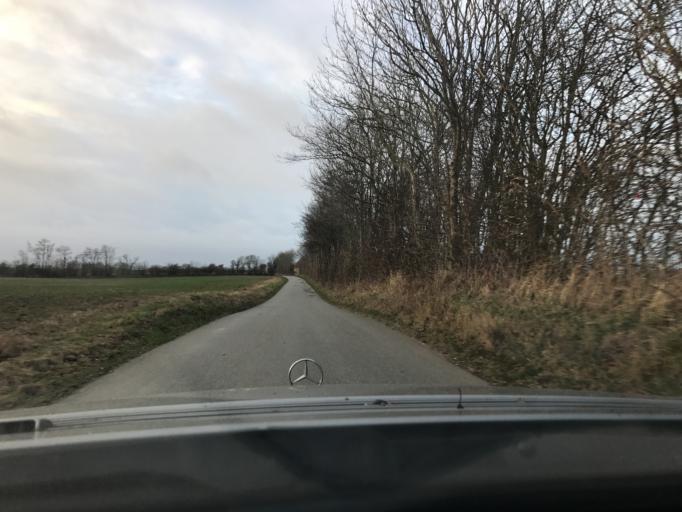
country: DK
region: South Denmark
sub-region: Sonderborg Kommune
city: Nordborg
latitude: 55.0529
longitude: 9.6828
